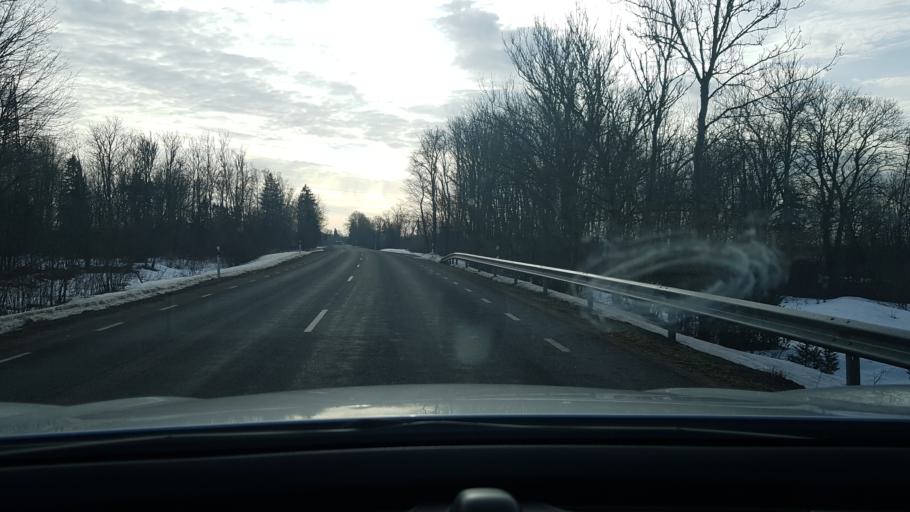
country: EE
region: Saare
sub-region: Kuressaare linn
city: Kuressaare
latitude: 58.2994
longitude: 22.5398
